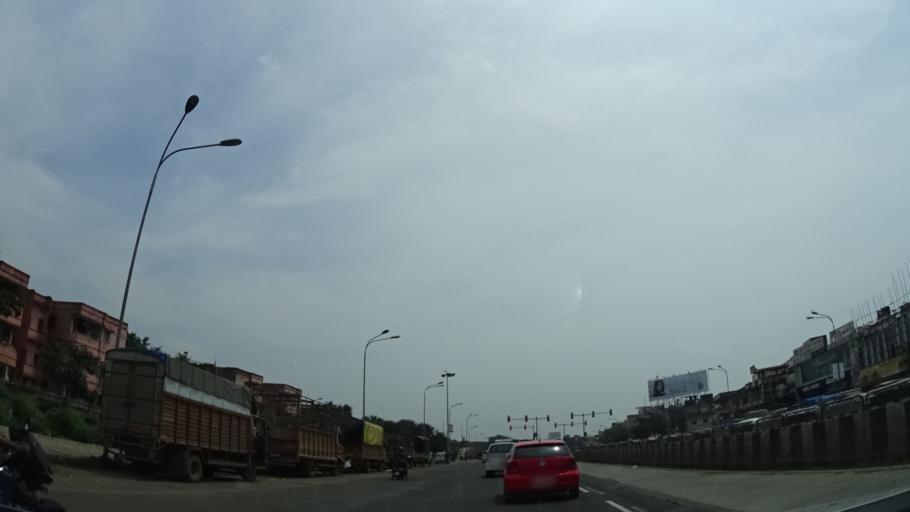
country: IN
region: Maharashtra
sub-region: Pune Division
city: Lohogaon
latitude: 18.5632
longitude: 73.9312
